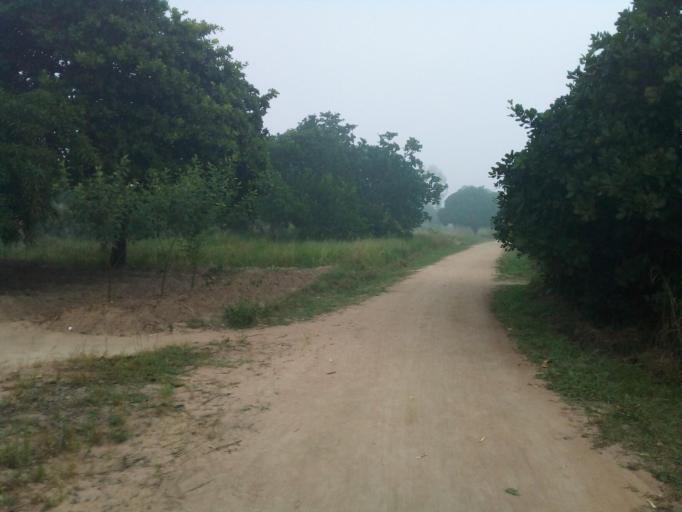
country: MZ
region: Zambezia
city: Quelimane
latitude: -17.5948
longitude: 36.6870
